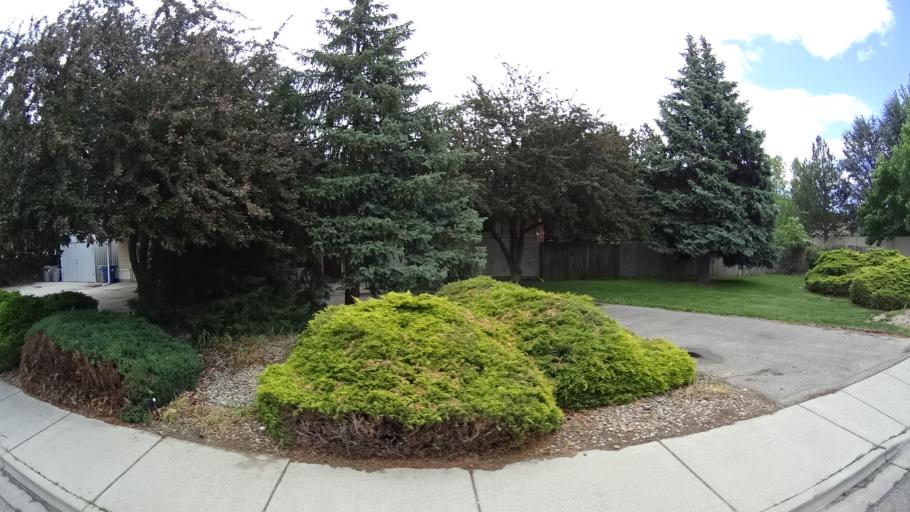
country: US
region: Idaho
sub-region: Ada County
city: Boise
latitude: 43.5753
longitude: -116.1734
